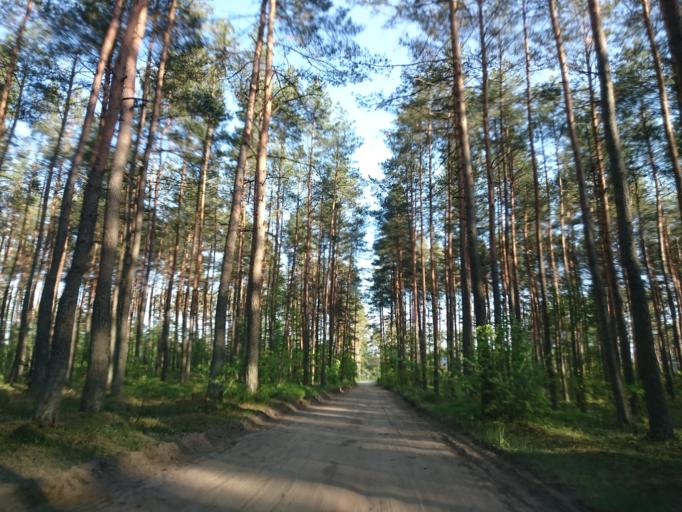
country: LV
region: Stopini
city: Ulbroka
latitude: 56.9499
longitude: 24.3507
